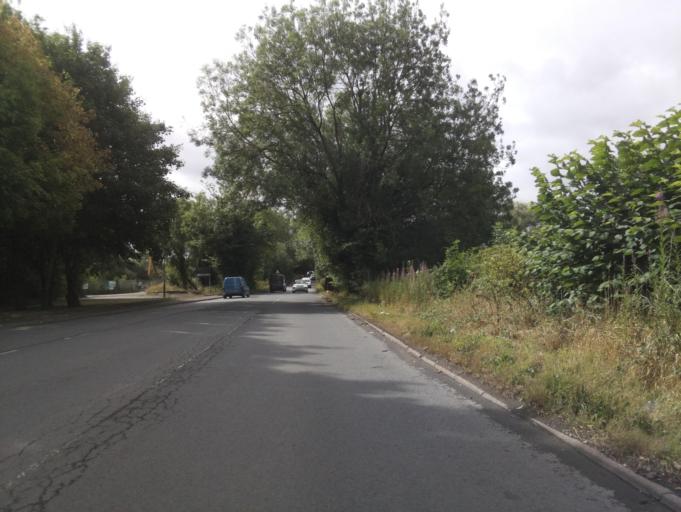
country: GB
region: England
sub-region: Derbyshire
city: Ilkeston
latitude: 52.9533
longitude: -1.3071
